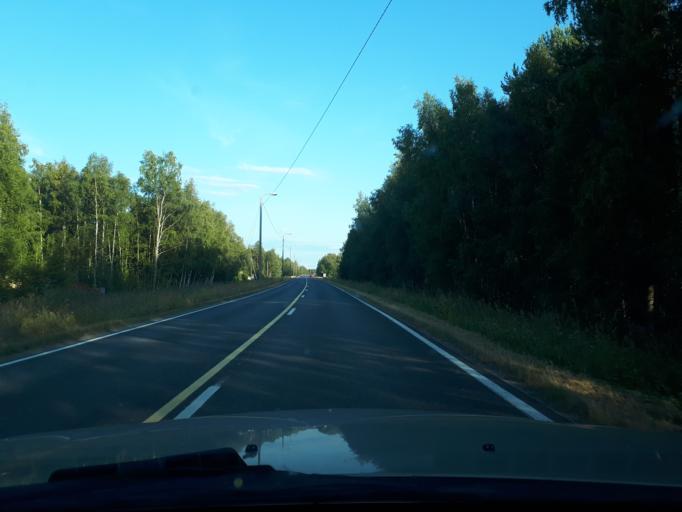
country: FI
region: Northern Ostrobothnia
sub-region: Oulu
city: Oulunsalo
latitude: 64.9868
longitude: 25.2606
